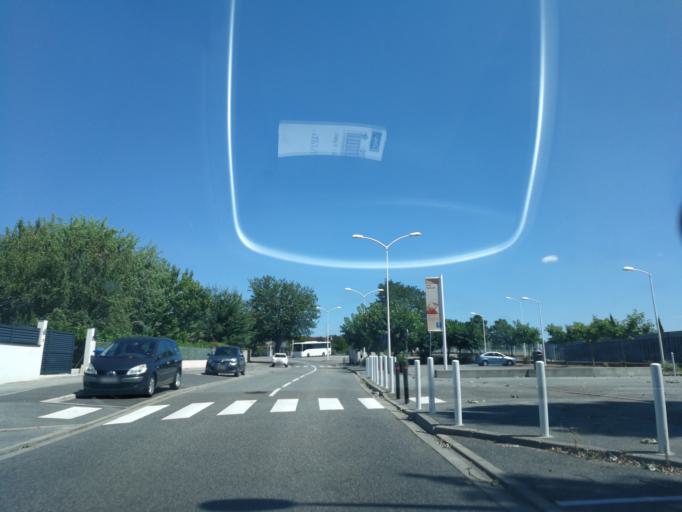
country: FR
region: Midi-Pyrenees
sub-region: Departement de la Haute-Garonne
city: Balma
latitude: 43.6042
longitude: 1.5064
